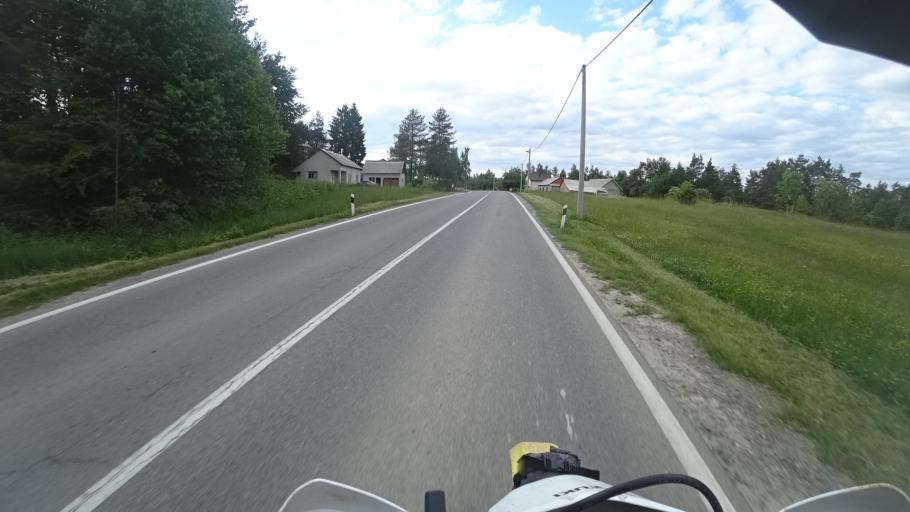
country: HR
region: Licko-Senjska
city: Gospic
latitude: 44.5211
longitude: 15.4150
